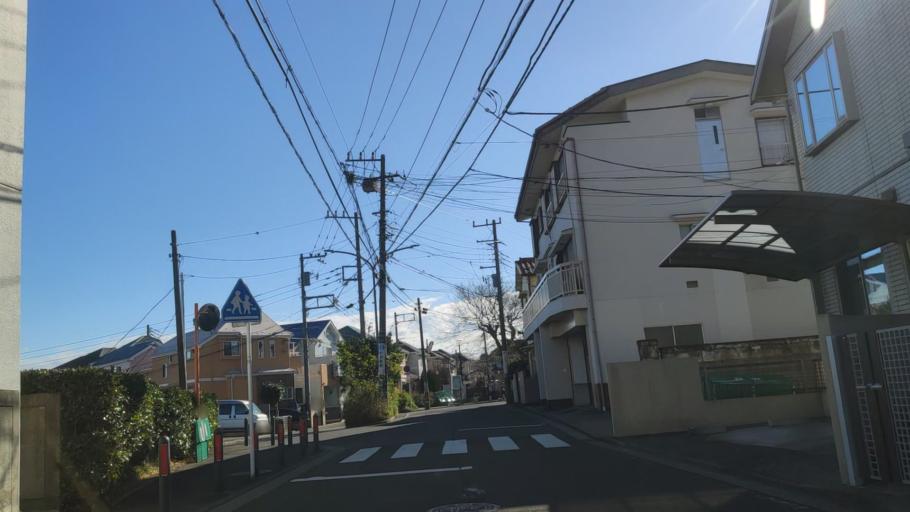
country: JP
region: Kanagawa
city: Yokohama
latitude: 35.4264
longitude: 139.6485
